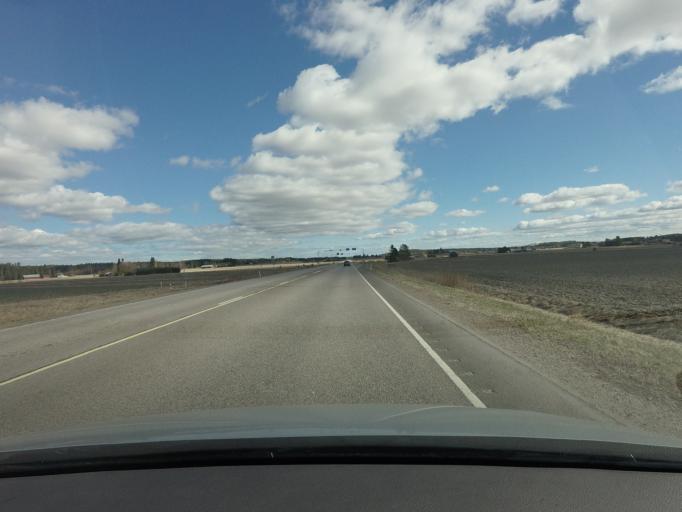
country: FI
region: Kymenlaakso
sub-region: Kouvola
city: Elimaeki
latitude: 60.7411
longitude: 26.4464
